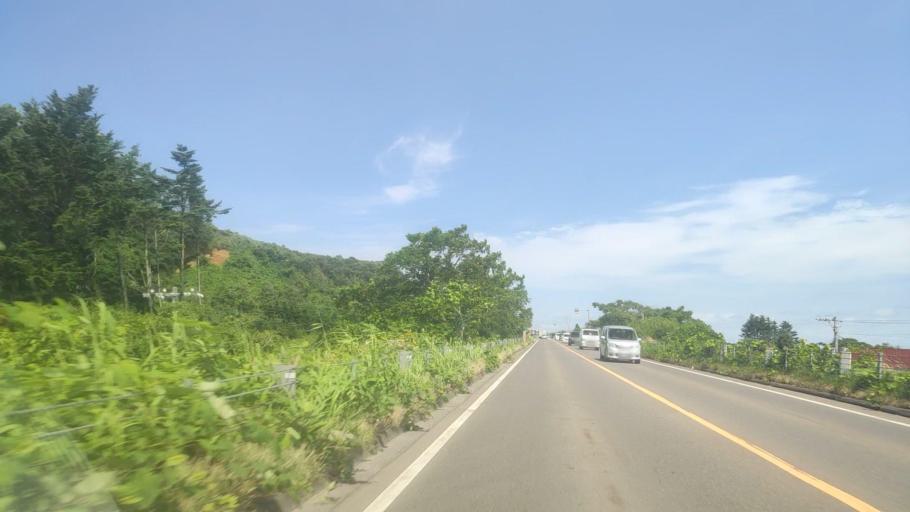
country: JP
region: Hokkaido
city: Nanae
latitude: 42.1938
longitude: 140.4199
